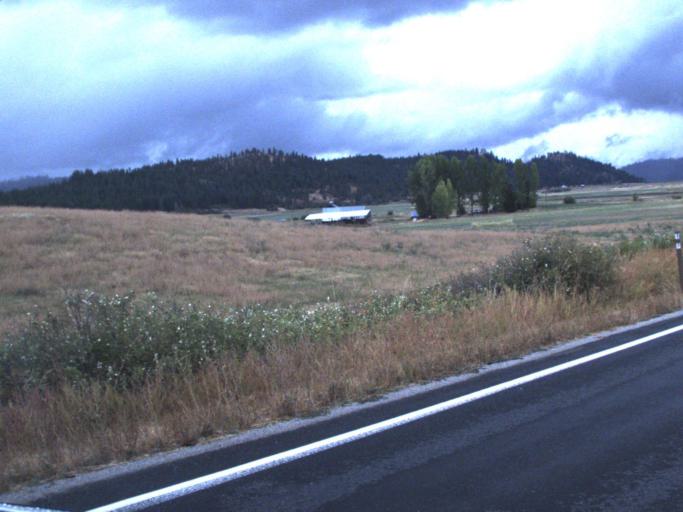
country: US
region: Washington
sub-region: Stevens County
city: Chewelah
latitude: 48.1193
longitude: -117.7535
